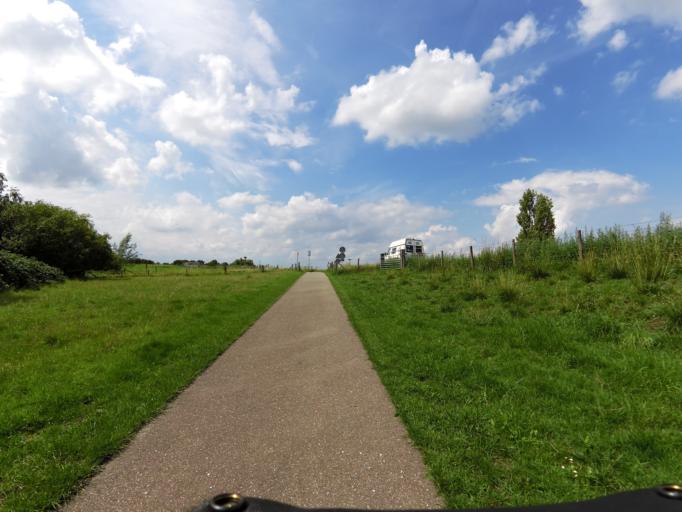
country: NL
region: South Holland
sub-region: Gemeente Strijen
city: Strijen
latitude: 51.7154
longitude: 4.5676
